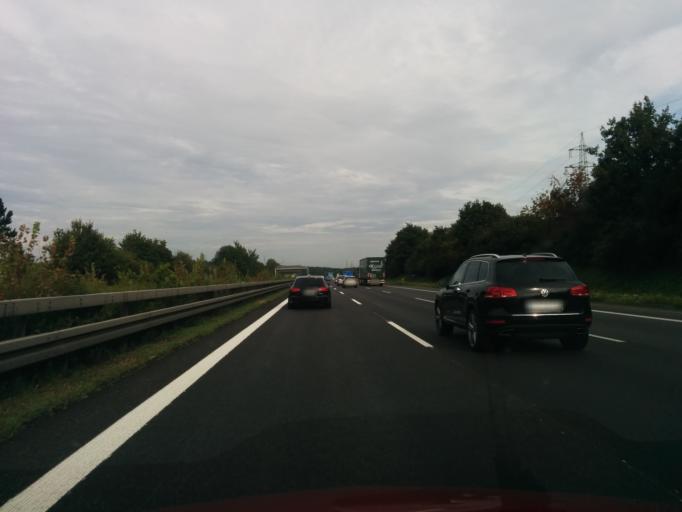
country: DE
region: Baden-Wuerttemberg
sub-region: Regierungsbezirk Stuttgart
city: Kirchheim unter Teck
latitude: 48.6428
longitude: 9.4279
